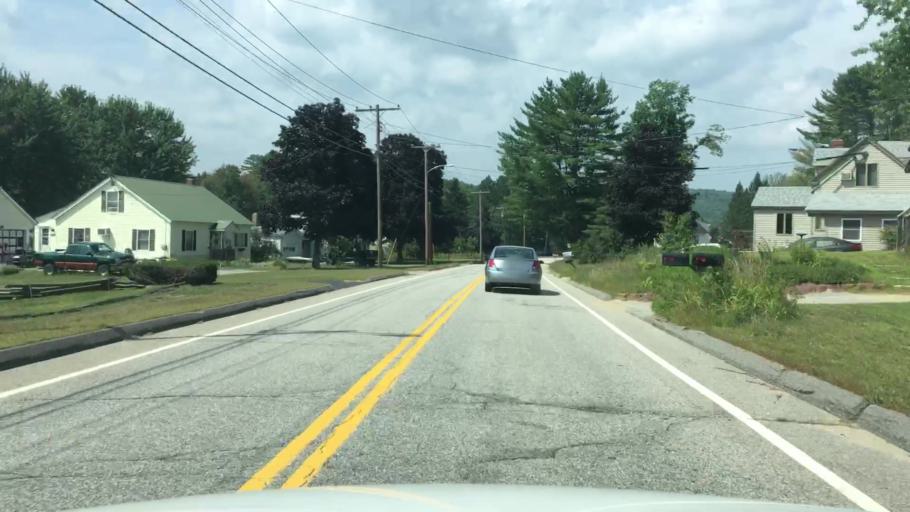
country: US
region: Maine
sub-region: Oxford County
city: Rumford
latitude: 44.5209
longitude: -70.5308
